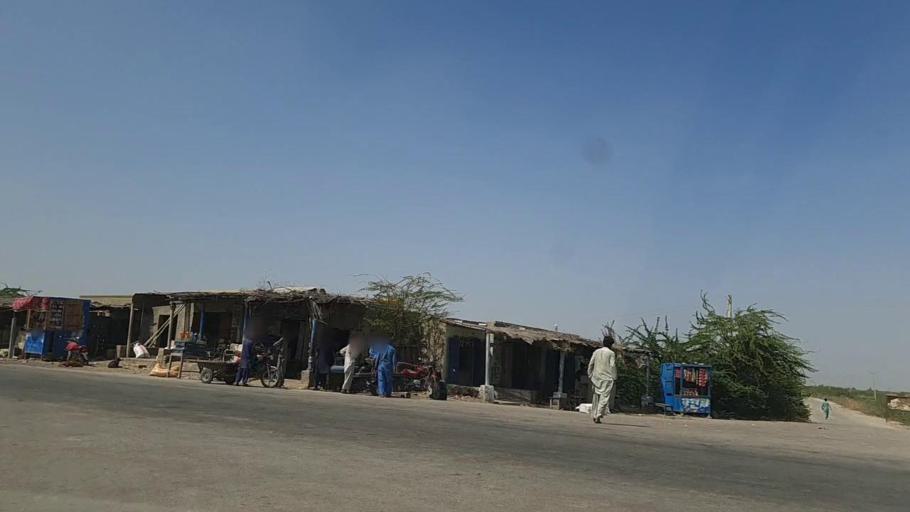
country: PK
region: Sindh
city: Naukot
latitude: 24.6240
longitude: 69.2890
